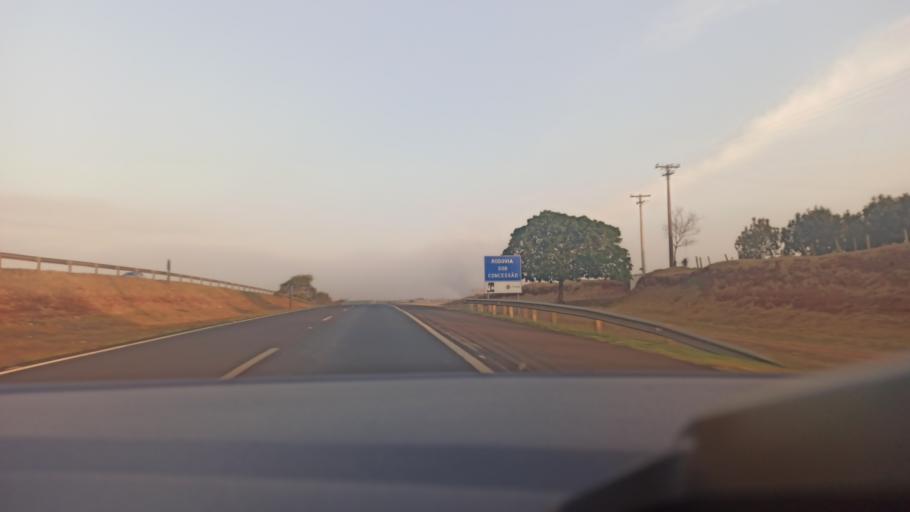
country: BR
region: Sao Paulo
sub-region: Taquaritinga
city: Taquaritinga
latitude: -21.4222
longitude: -48.6761
